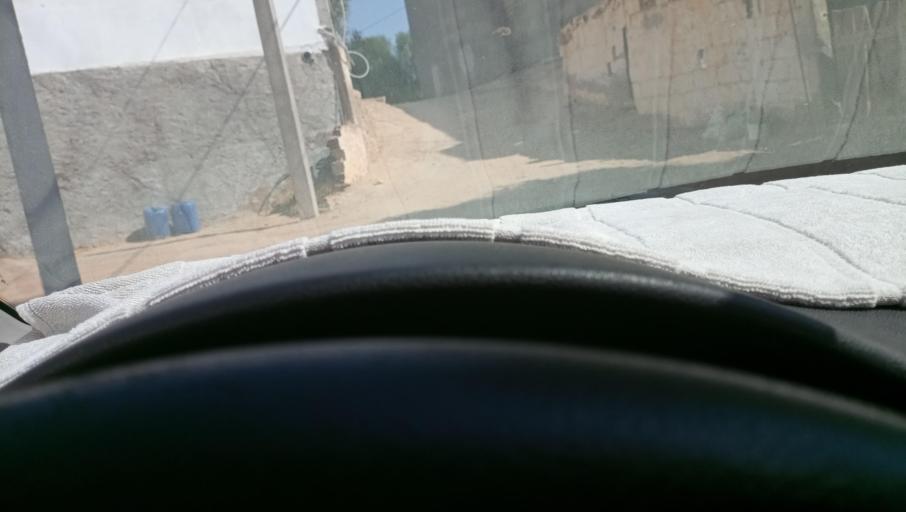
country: TN
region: Tataouine
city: Tataouine
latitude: 32.9821
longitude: 10.3812
